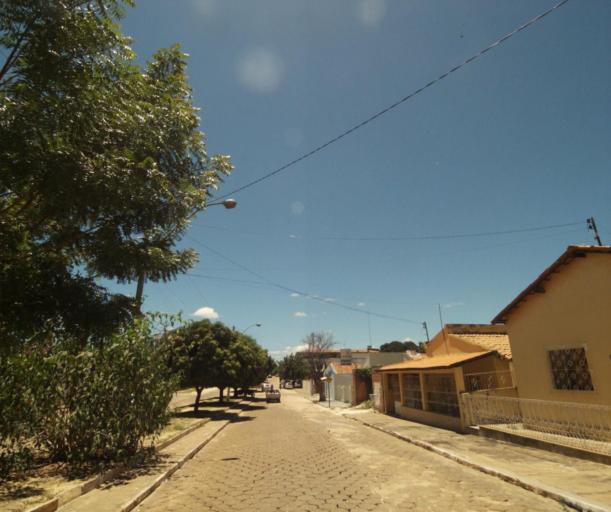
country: BR
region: Bahia
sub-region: Carinhanha
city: Carinhanha
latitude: -14.3001
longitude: -43.7702
